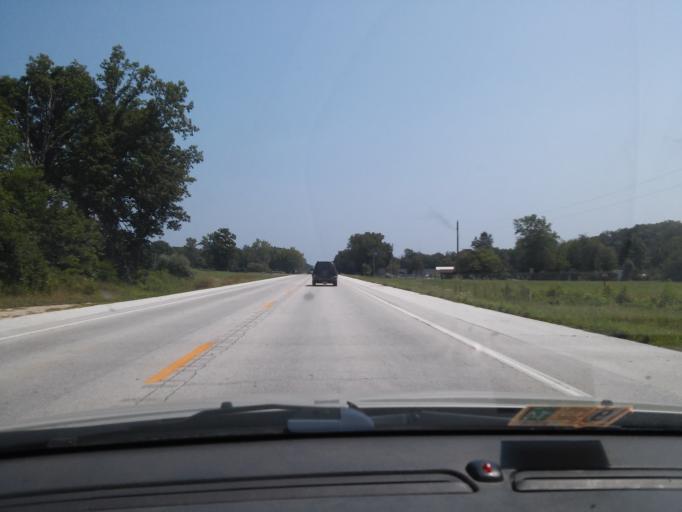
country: US
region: Missouri
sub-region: Pike County
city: Bowling Green
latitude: 39.3721
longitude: -91.1667
